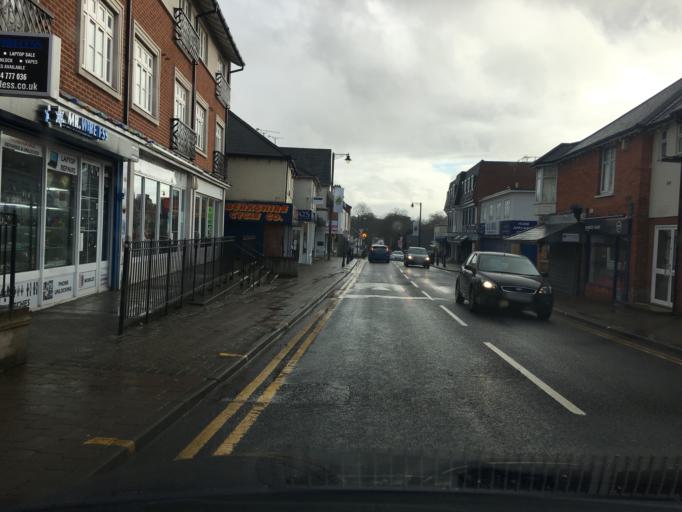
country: GB
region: England
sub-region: Bracknell Forest
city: Crowthorne
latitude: 51.3680
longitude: -0.7937
